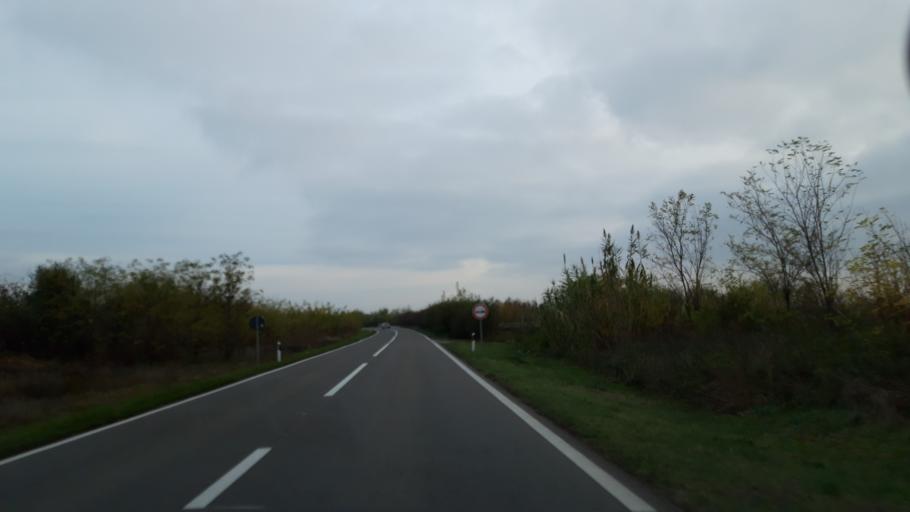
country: RS
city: Sanad
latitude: 45.9674
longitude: 20.1250
